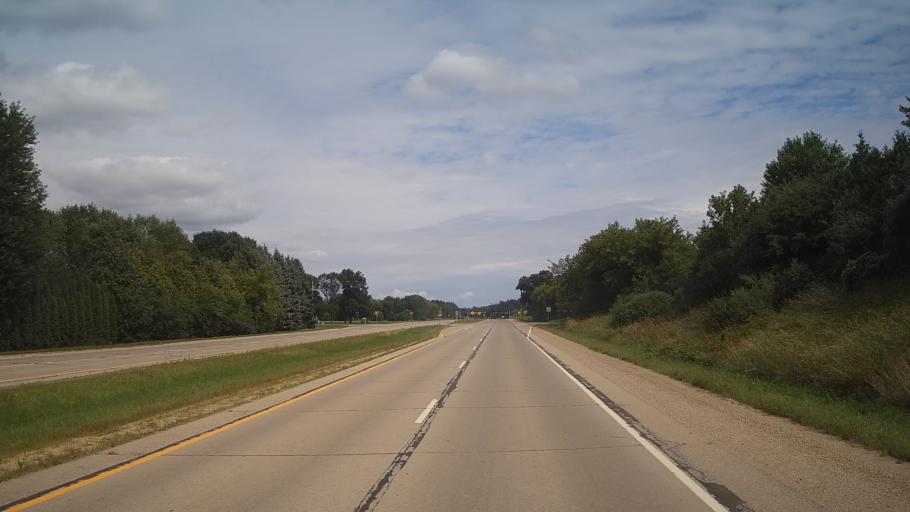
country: US
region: Wisconsin
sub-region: Winnebago County
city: Oshkosh
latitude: 44.0290
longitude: -88.6119
